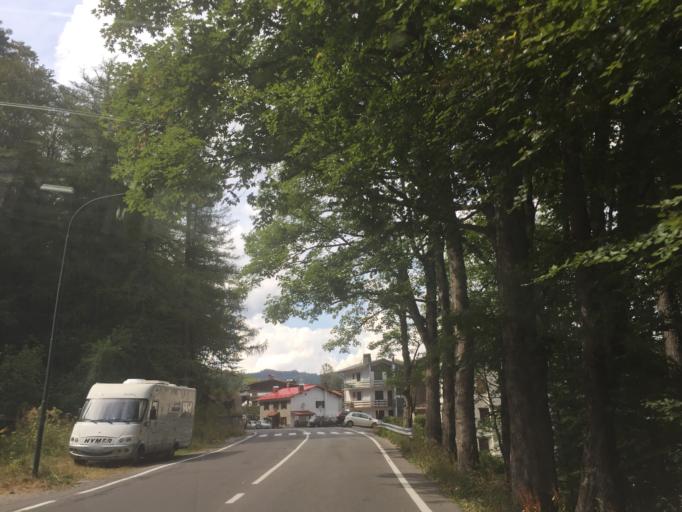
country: IT
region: Tuscany
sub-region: Provincia di Pistoia
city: Abetone
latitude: 44.1292
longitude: 10.6888
